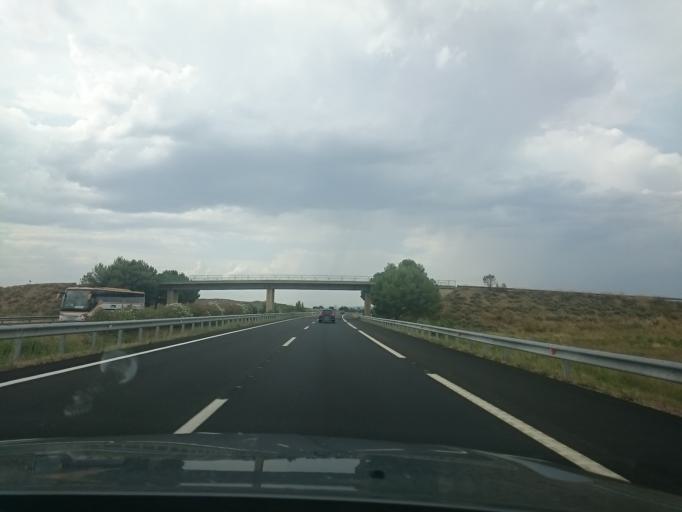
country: ES
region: La Rioja
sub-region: Provincia de La Rioja
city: Aldeanueva de Ebro
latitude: 42.2302
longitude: -1.9002
